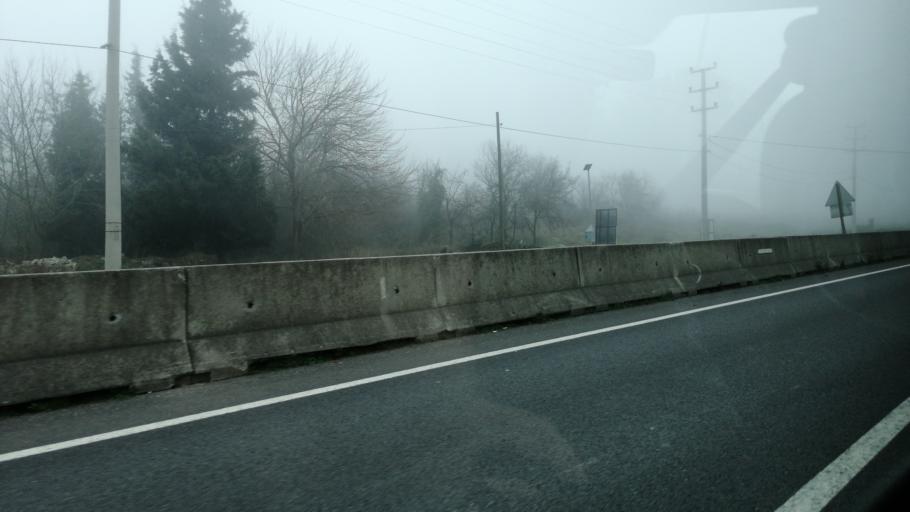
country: TR
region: Yalova
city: Ciftlikkoy
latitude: 40.6763
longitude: 29.3495
